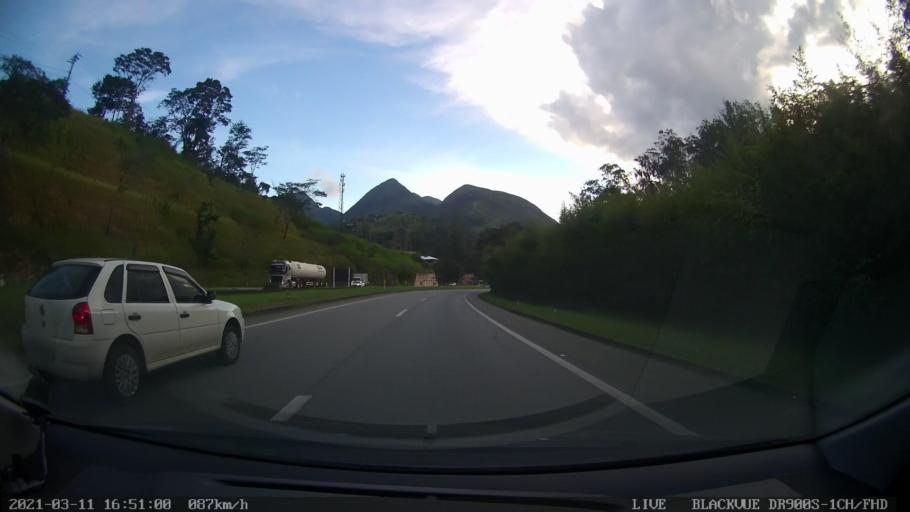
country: BR
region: Rio de Janeiro
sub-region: Petropolis
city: Petropolis
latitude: -22.4324
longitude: -43.1701
